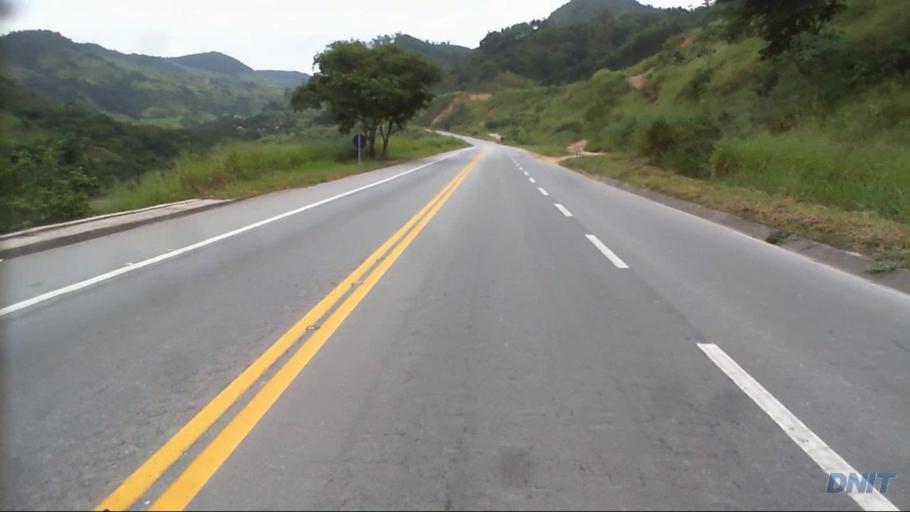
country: BR
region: Minas Gerais
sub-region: Timoteo
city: Timoteo
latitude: -19.6222
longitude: -42.8037
